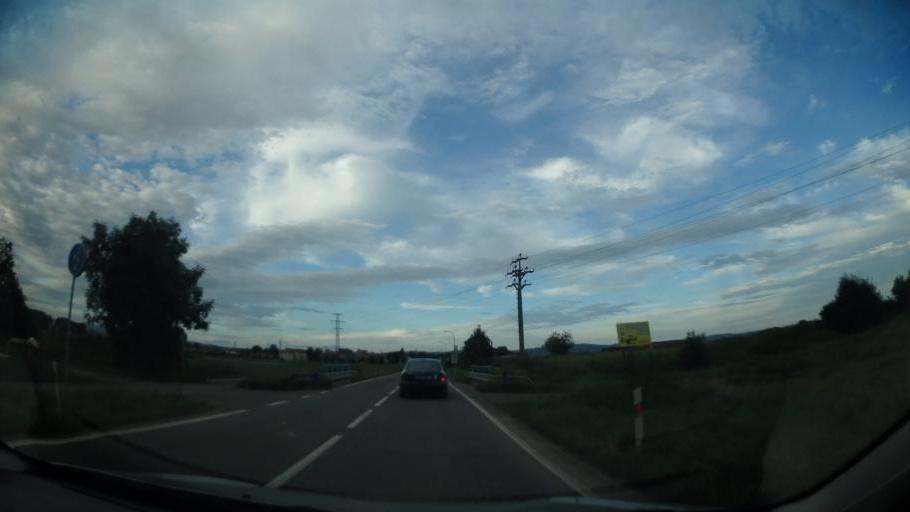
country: CZ
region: Olomoucky
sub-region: Okres Olomouc
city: Unicov
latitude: 49.7621
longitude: 17.1063
